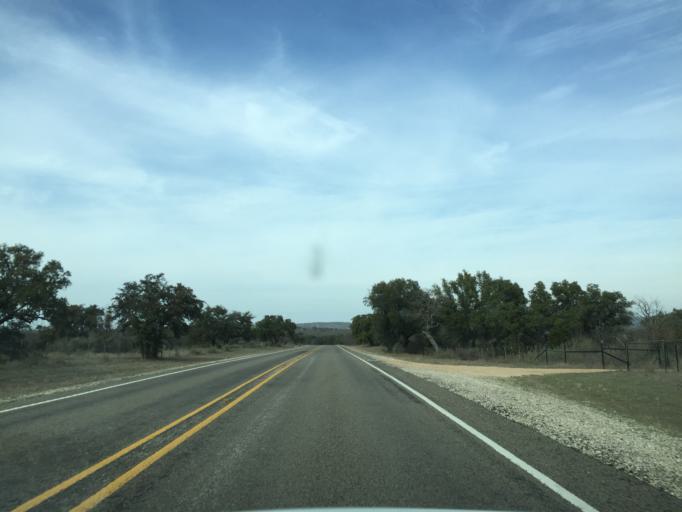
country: US
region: Texas
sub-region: Llano County
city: Llano
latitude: 30.5229
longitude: -98.7073
